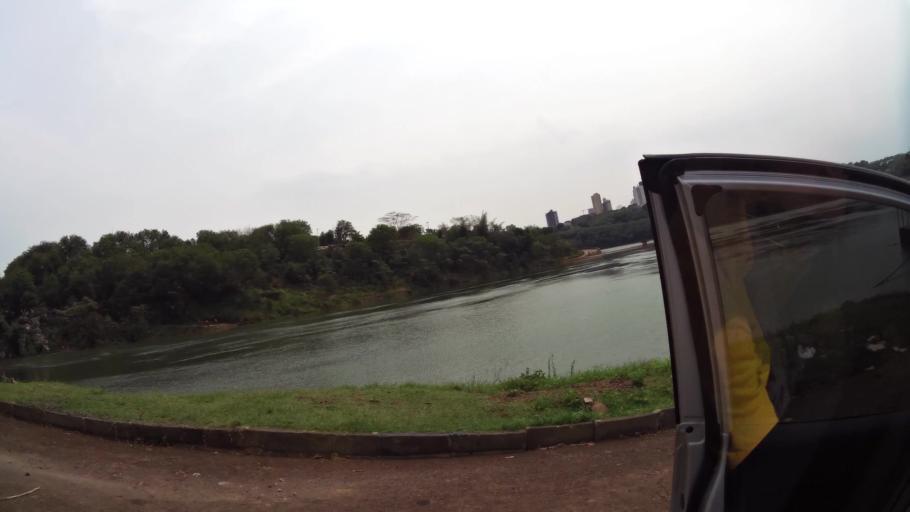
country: BR
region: Parana
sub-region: Foz Do Iguacu
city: Foz do Iguacu
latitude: -25.5553
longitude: -54.5980
